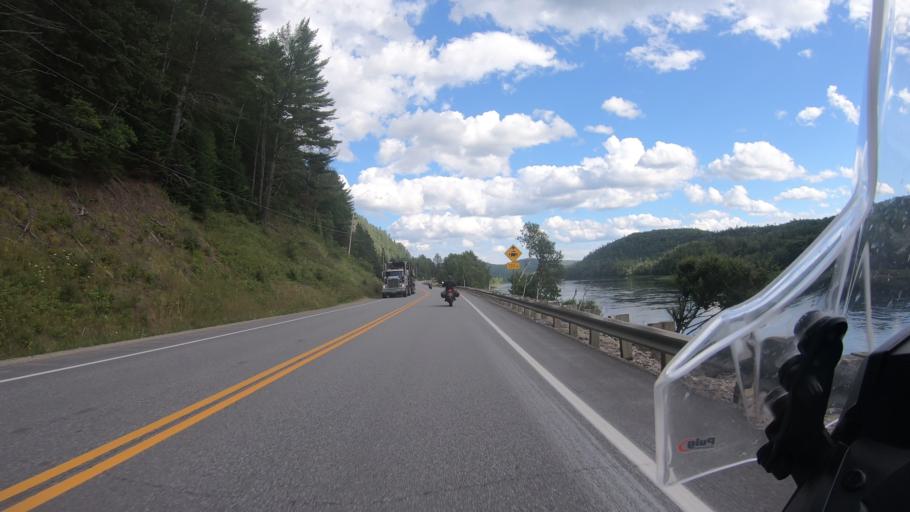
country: CA
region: Quebec
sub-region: Mauricie
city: Saint-Tite
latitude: 46.9942
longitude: -72.9169
